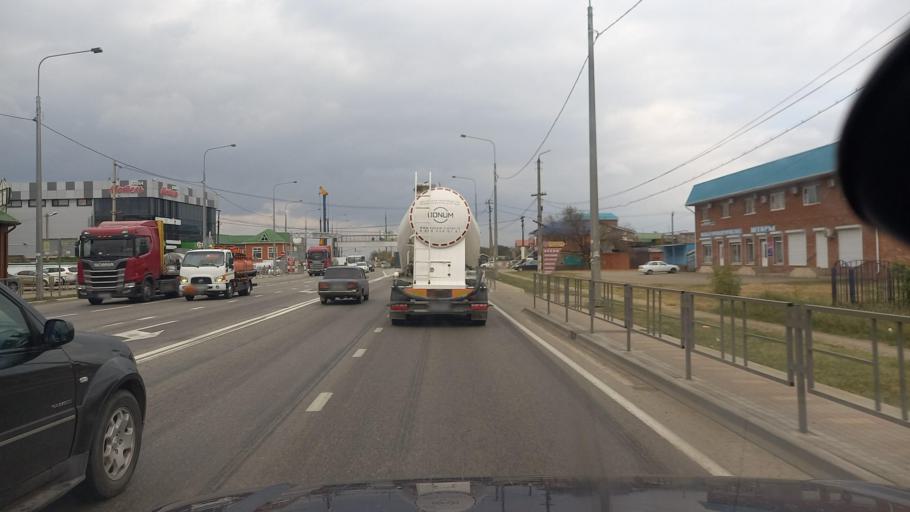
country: RU
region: Adygeya
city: Enem
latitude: 44.9309
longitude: 38.9108
